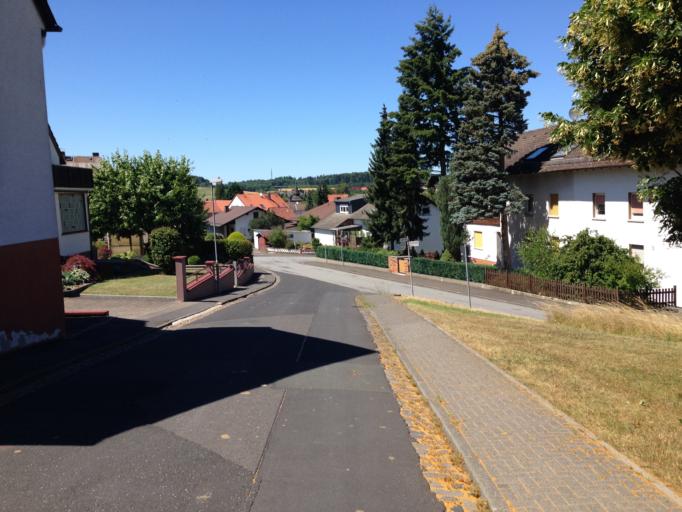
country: DE
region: Hesse
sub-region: Regierungsbezirk Giessen
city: Reiskirchen
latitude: 50.5940
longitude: 8.8369
